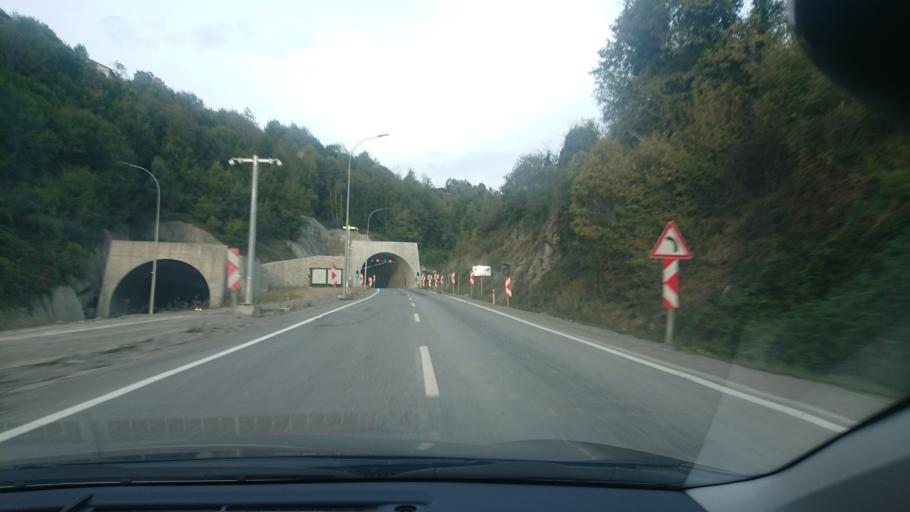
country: TR
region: Zonguldak
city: Beycuma
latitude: 41.4119
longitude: 31.9221
